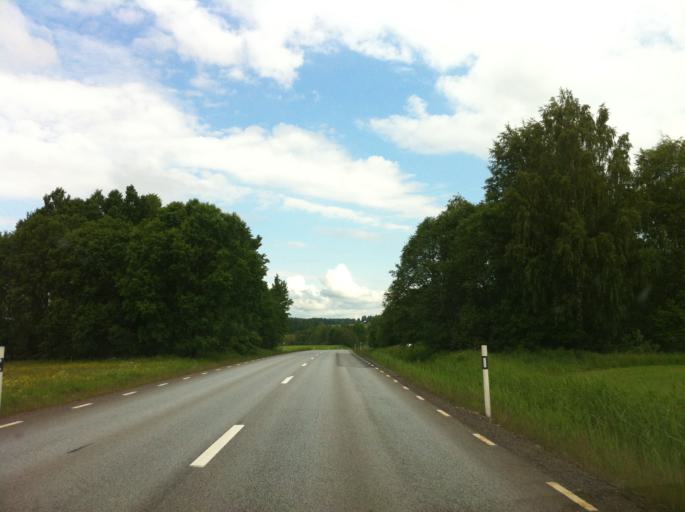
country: SE
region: Vaermland
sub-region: Sunne Kommun
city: Sunne
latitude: 59.7211
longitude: 13.1356
